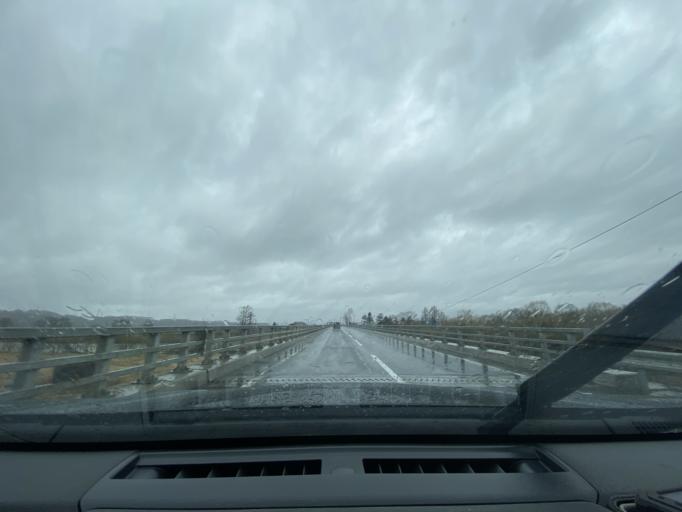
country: JP
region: Hokkaido
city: Fukagawa
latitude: 43.8091
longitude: 142.0160
